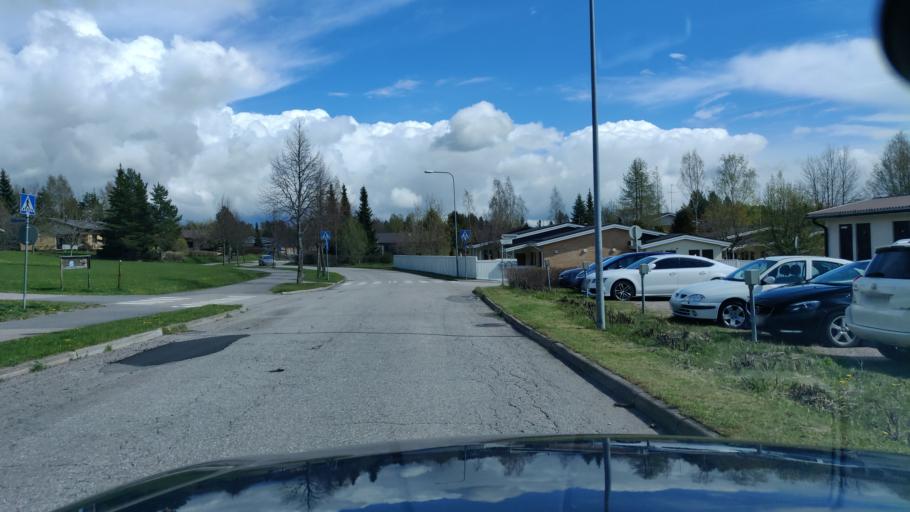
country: FI
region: Uusimaa
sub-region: Helsinki
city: Nurmijaervi
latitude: 60.3667
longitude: 24.7385
